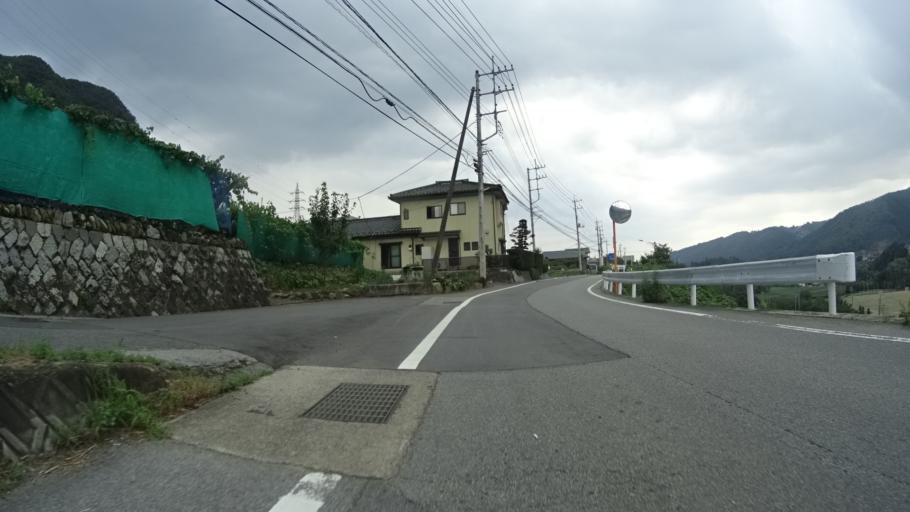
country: JP
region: Yamanashi
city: Enzan
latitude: 35.7411
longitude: 138.7221
